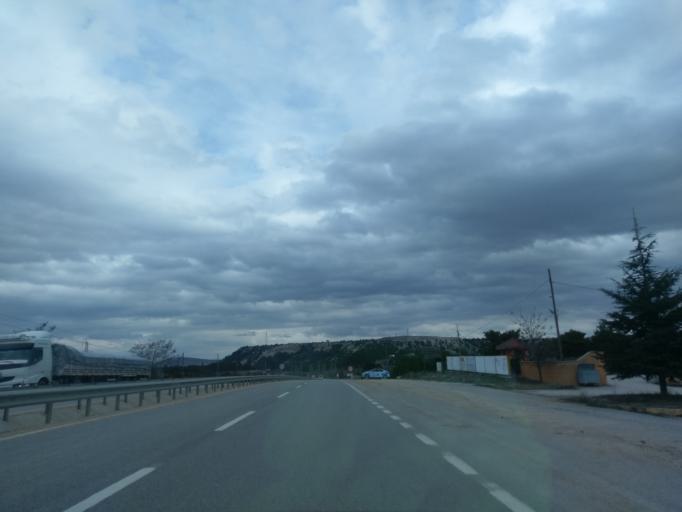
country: TR
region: Eskisehir
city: Eskisehir
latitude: 39.7251
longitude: 30.3376
